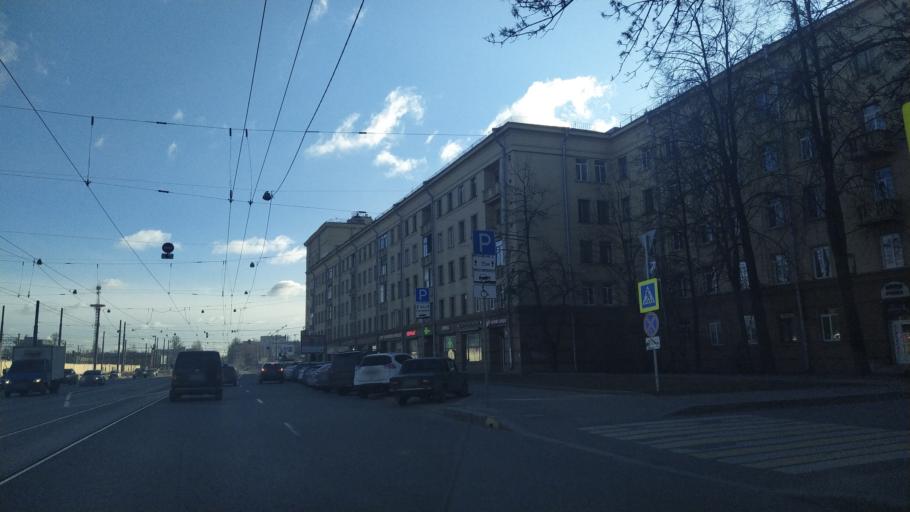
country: RU
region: Leningrad
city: Sampsonievskiy
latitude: 59.9731
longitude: 30.3473
